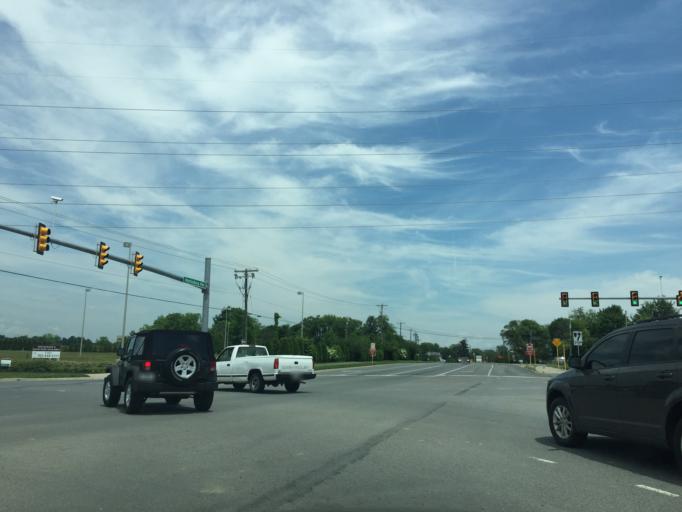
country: US
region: Virginia
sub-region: City of Winchester
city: Winchester
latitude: 39.2195
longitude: -78.1327
